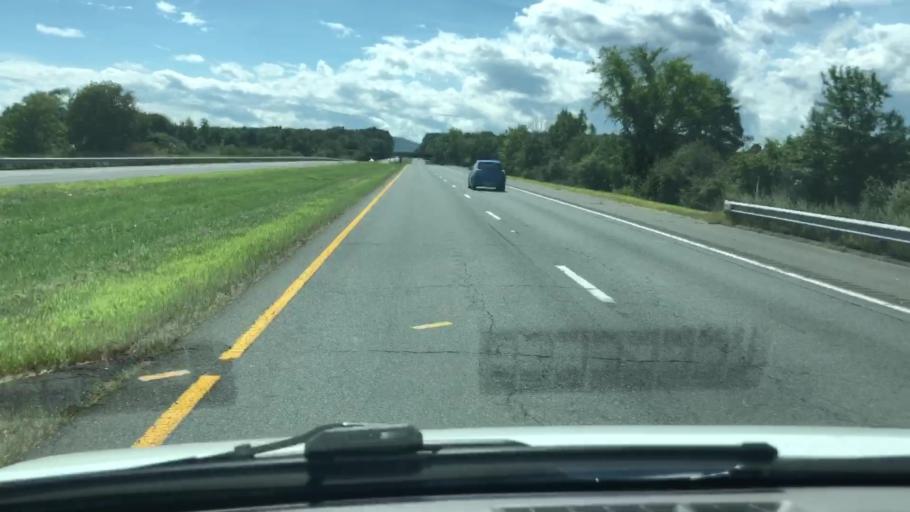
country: US
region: Massachusetts
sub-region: Hampshire County
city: Amherst Center
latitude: 42.3776
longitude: -72.5410
